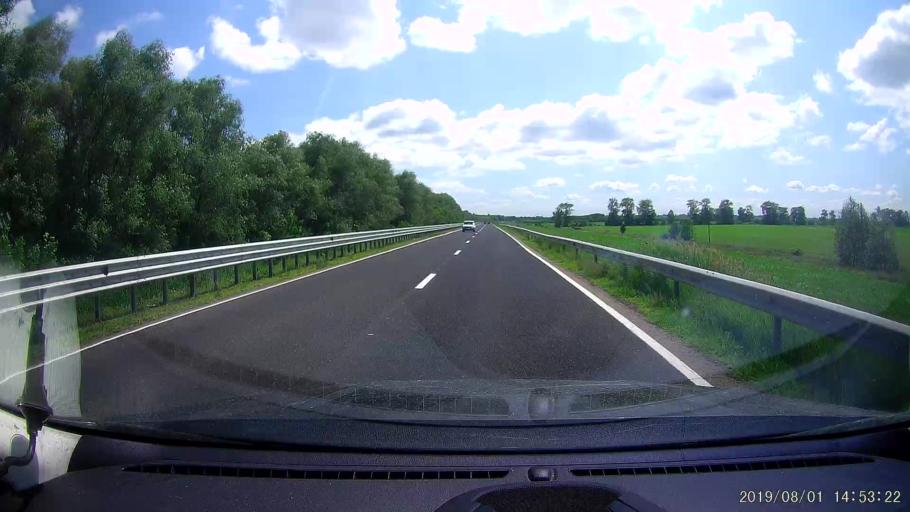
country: RO
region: Braila
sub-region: Municipiul Braila
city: Braila
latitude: 45.3369
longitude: 28.0040
